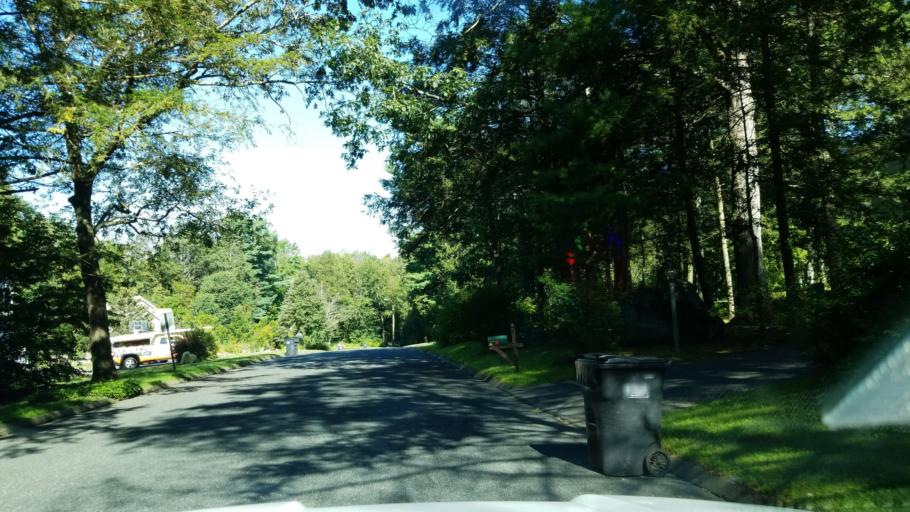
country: US
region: Connecticut
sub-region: Tolland County
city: Somers
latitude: 41.9784
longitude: -72.4151
